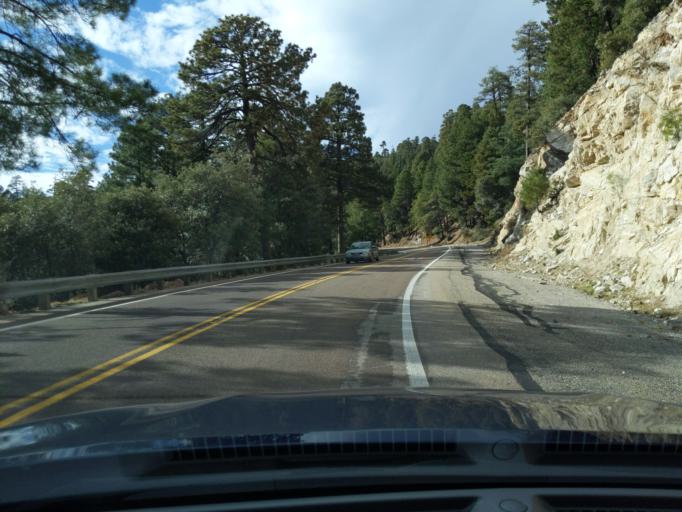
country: US
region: Arizona
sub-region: Pima County
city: Tanque Verde
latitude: 32.4097
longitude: -110.7069
